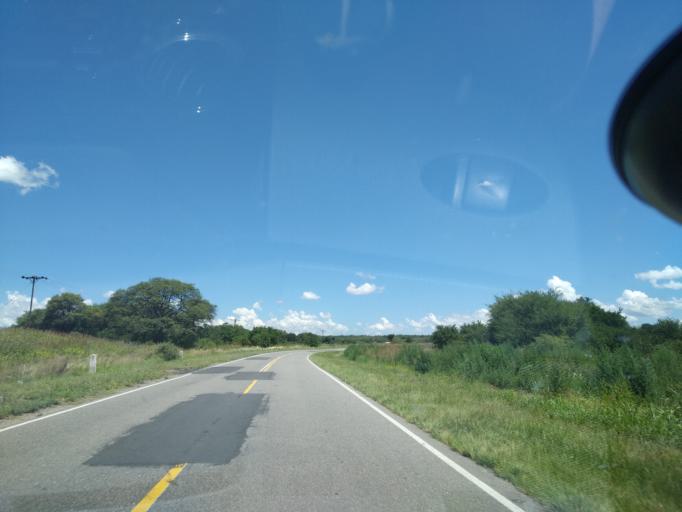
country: AR
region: Cordoba
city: Salsacate
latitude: -31.4178
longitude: -65.0947
